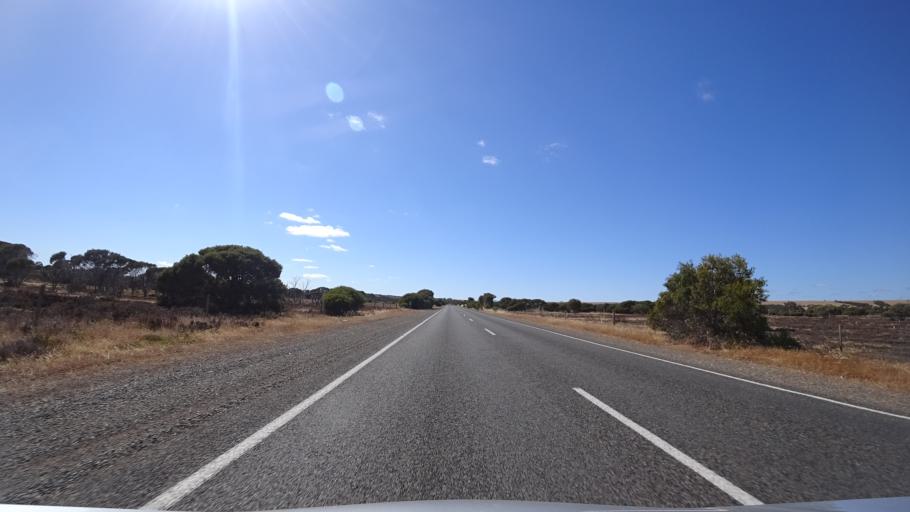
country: AU
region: South Australia
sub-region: Kangaroo Island
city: Kingscote
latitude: -35.7386
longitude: 137.5771
